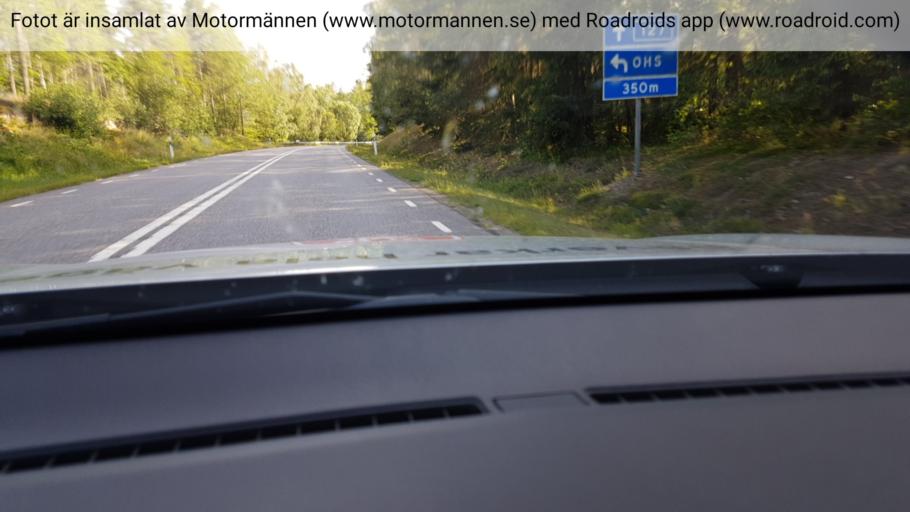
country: SE
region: Joenkoeping
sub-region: Varnamo Kommun
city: Bor
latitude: 57.2322
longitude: 14.1574
